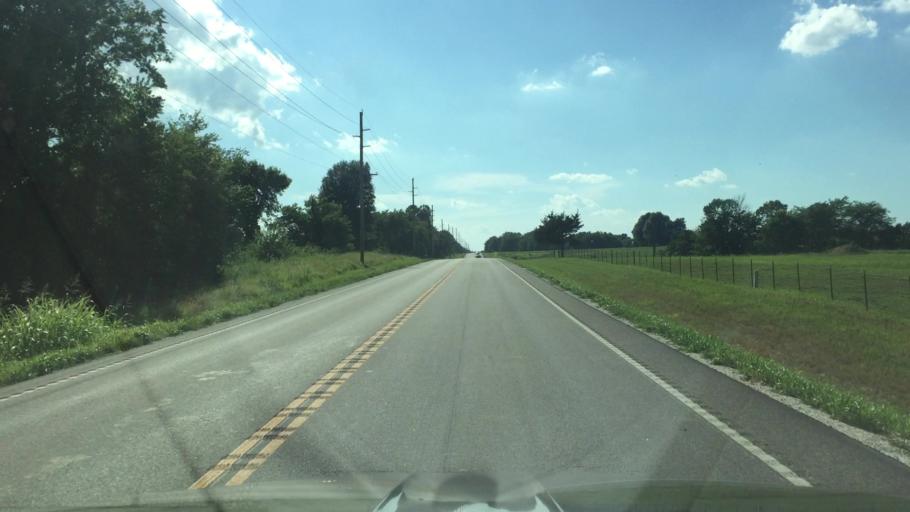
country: US
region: Missouri
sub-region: Morgan County
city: Versailles
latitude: 38.3959
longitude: -92.7228
